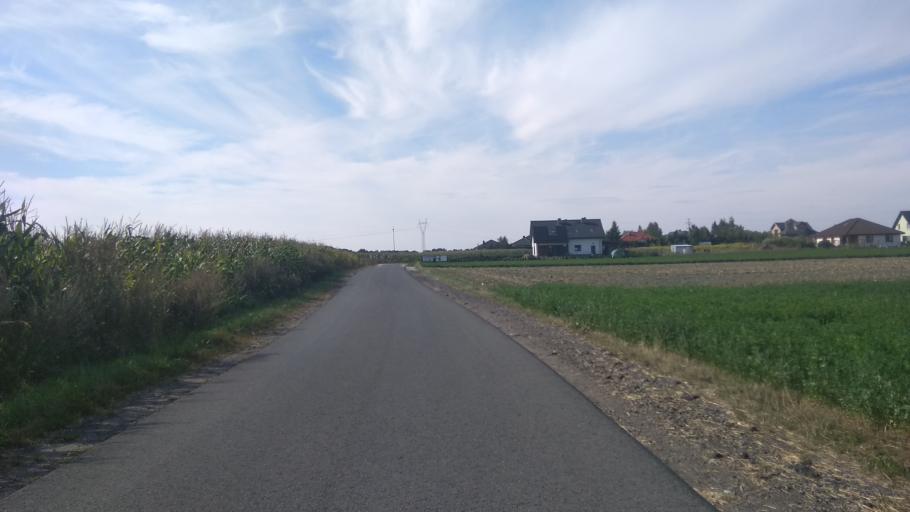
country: PL
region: Kujawsko-Pomorskie
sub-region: Bydgoszcz
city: Fordon
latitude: 53.2165
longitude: 18.1490
